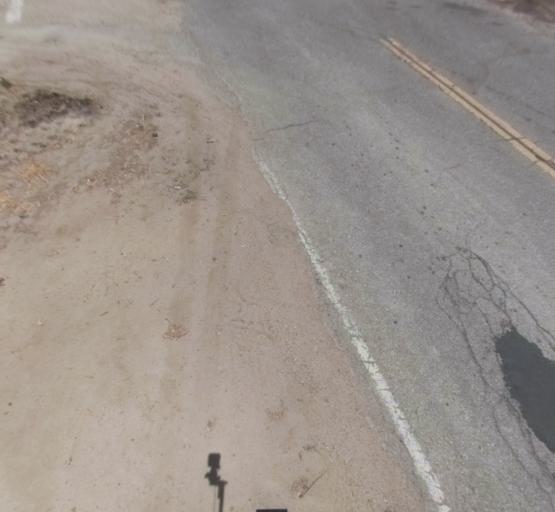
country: US
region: California
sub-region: Madera County
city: Madera
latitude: 36.9643
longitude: -120.0804
